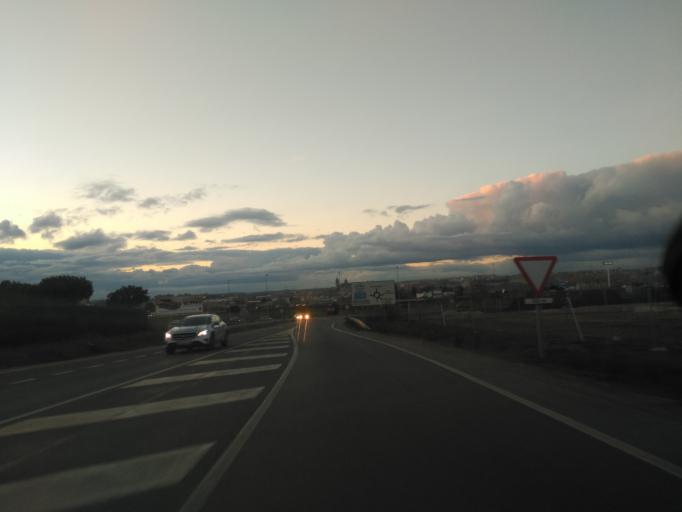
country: ES
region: Castille and Leon
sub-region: Provincia de Salamanca
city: Santa Marta de Tormes
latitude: 40.9392
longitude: -5.6347
